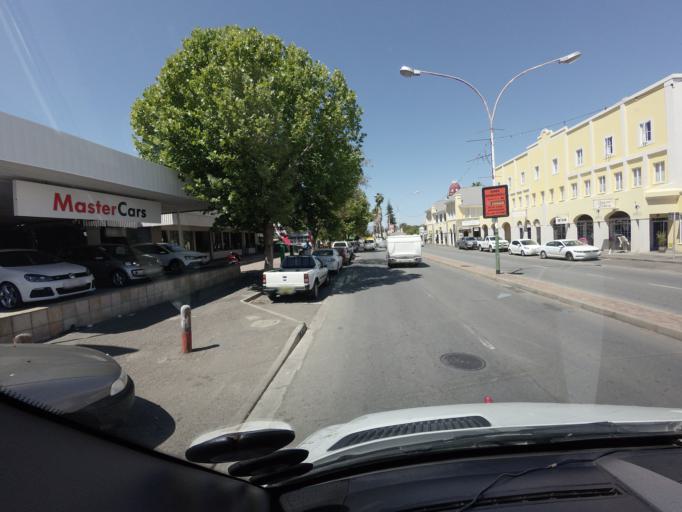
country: ZA
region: Western Cape
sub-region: Eden District Municipality
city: Oudtshoorn
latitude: -33.5909
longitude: 22.2029
